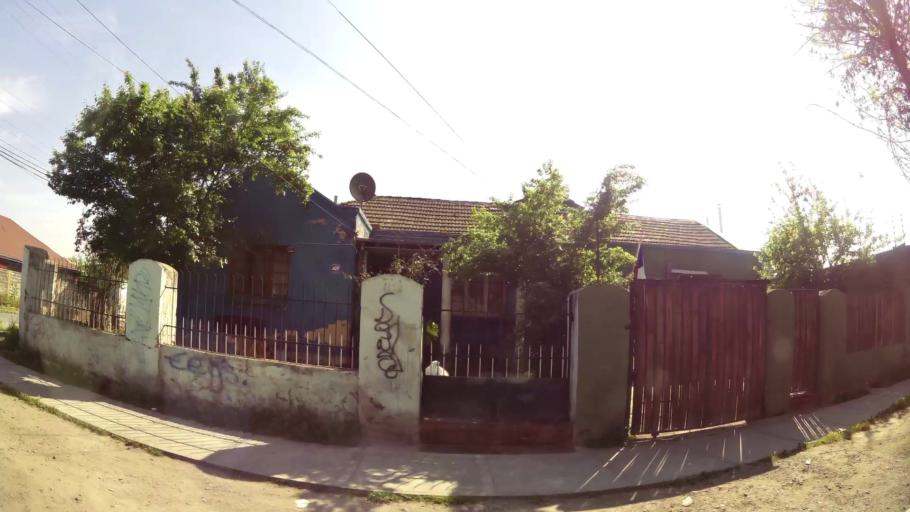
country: CL
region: Santiago Metropolitan
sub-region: Provincia de Maipo
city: San Bernardo
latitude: -33.5568
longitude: -70.6744
